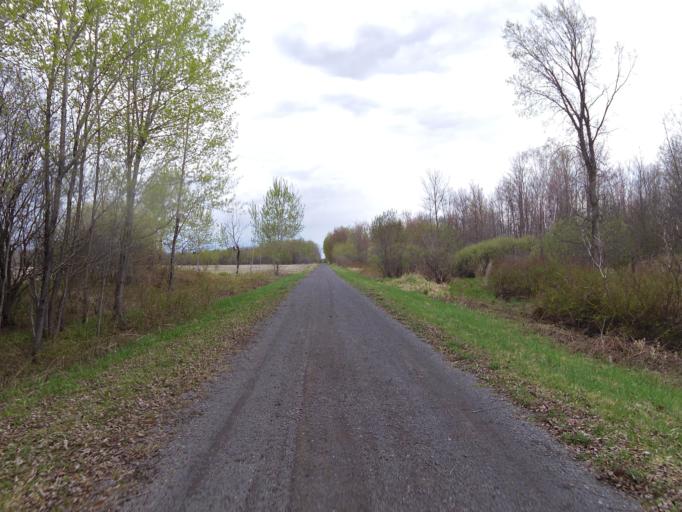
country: CA
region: Quebec
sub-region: Outaouais
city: Papineauville
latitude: 45.5180
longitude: -74.9528
